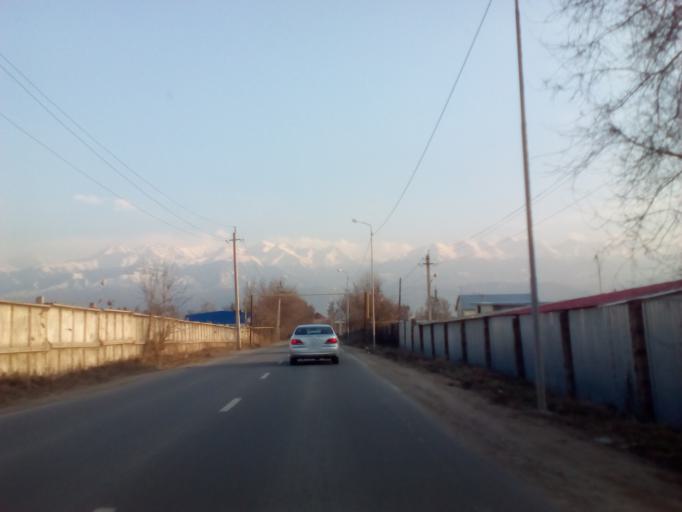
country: KZ
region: Almaty Oblysy
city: Burunday
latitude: 43.2318
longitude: 76.7412
